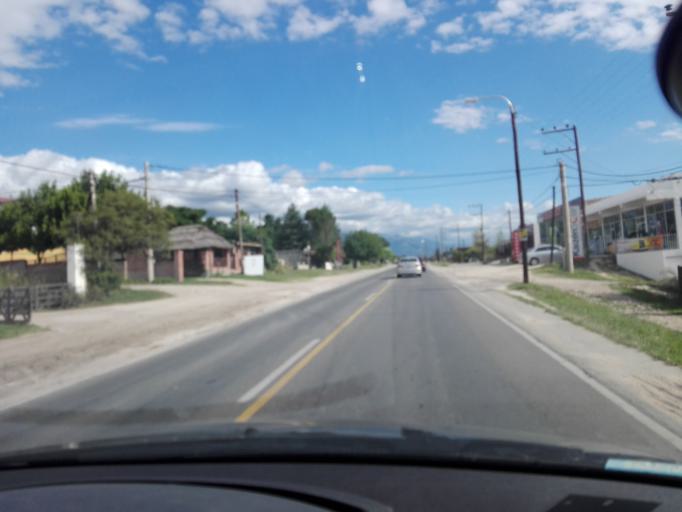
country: AR
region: Cordoba
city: Mina Clavero
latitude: -31.7537
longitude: -65.0029
